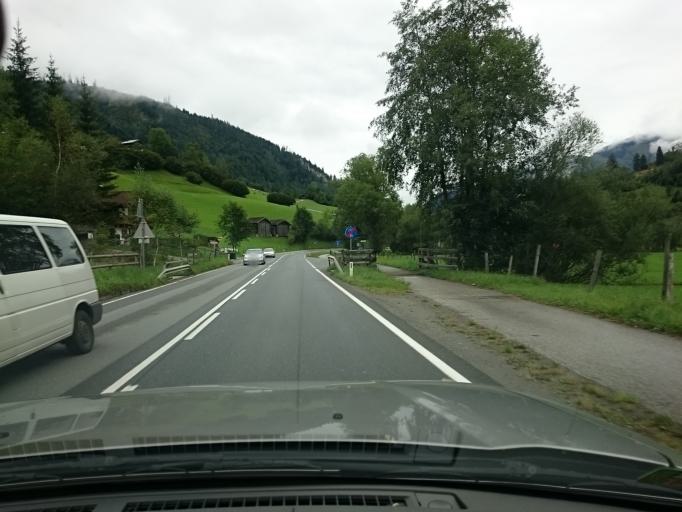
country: AT
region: Salzburg
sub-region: Politischer Bezirk Zell am See
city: Bruck an der Grossglocknerstrasse
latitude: 47.2574
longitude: 12.8250
